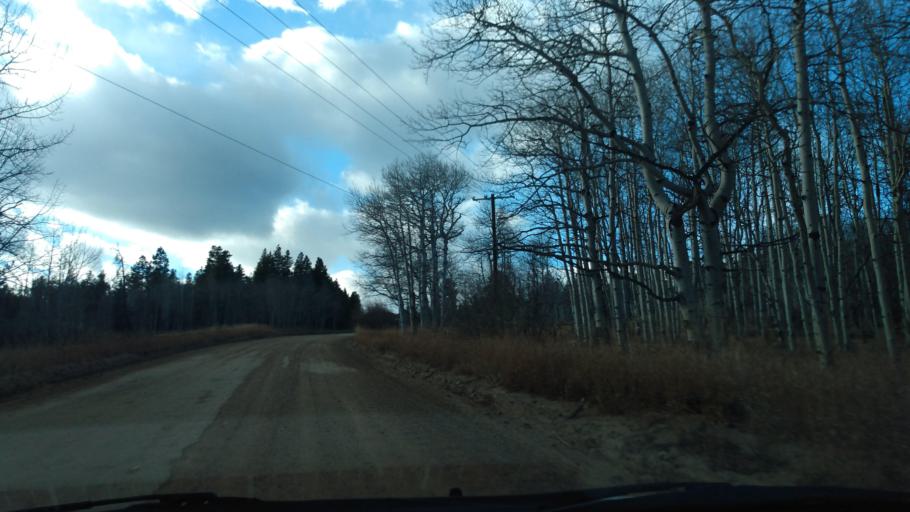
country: US
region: Colorado
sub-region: Boulder County
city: Nederland
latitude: 39.9535
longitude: -105.4576
